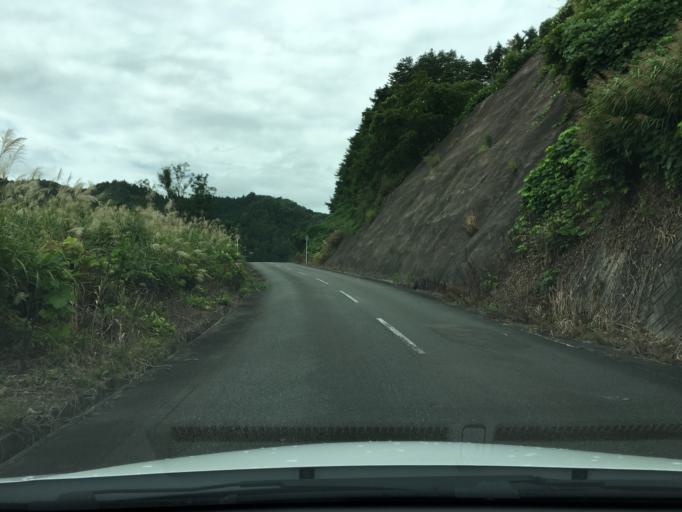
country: JP
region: Yamagata
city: Yonezawa
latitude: 37.8676
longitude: 140.1722
